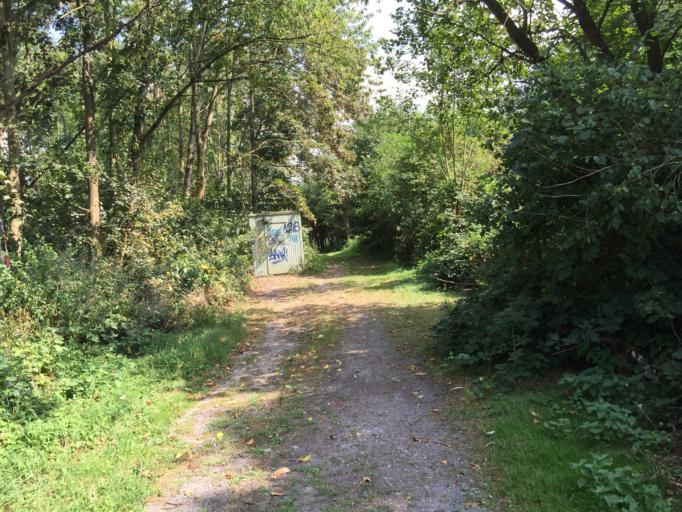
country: DE
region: North Rhine-Westphalia
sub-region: Regierungsbezirk Koln
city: Bergheim
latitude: 50.9616
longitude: 6.6231
